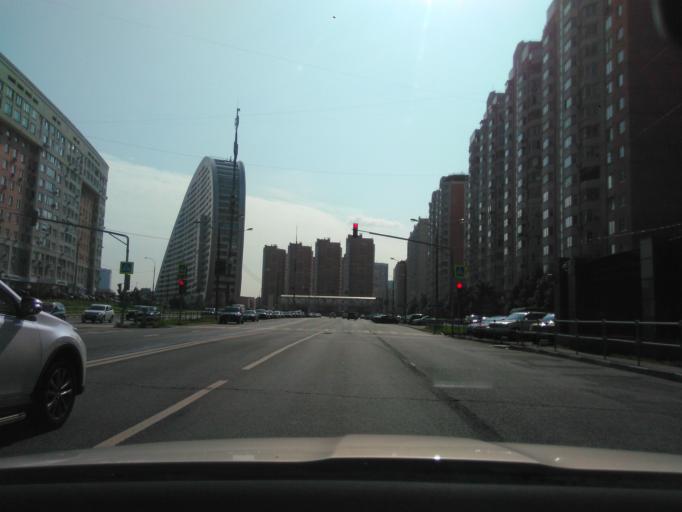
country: RU
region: Moscow
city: Sokol
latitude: 55.7829
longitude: 37.5261
